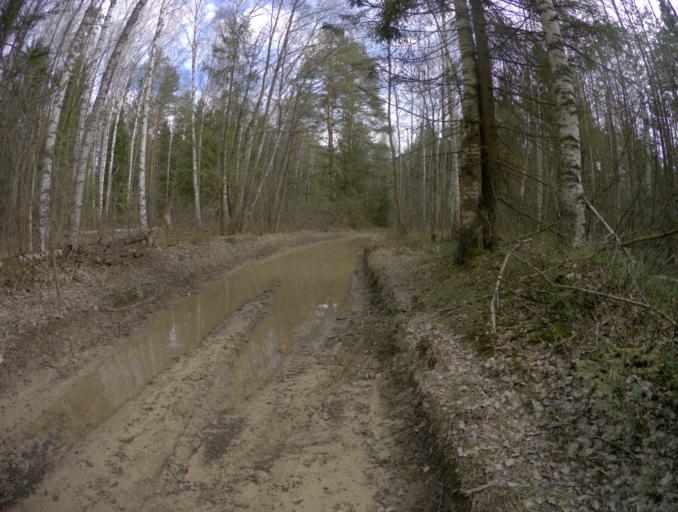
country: RU
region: Vladimir
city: Orgtrud
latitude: 56.0727
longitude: 40.7100
